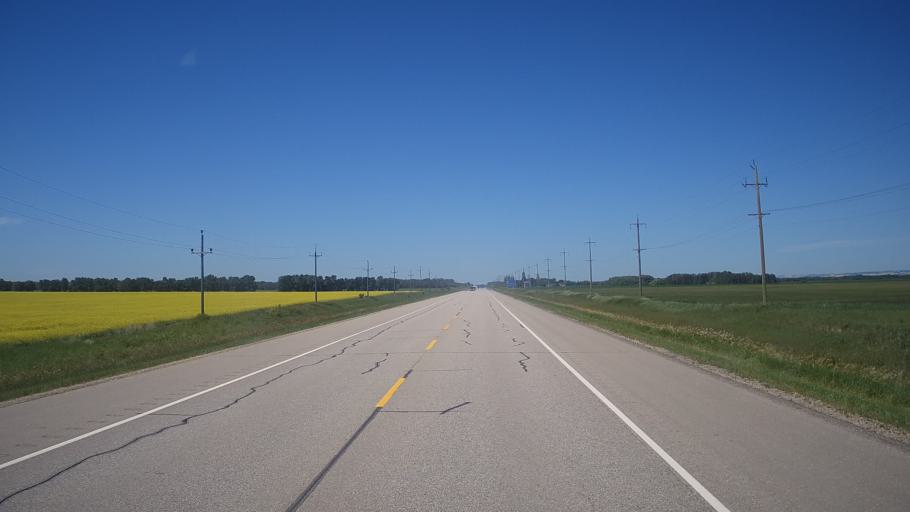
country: CA
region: Manitoba
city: Neepawa
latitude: 50.2253
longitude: -99.3218
